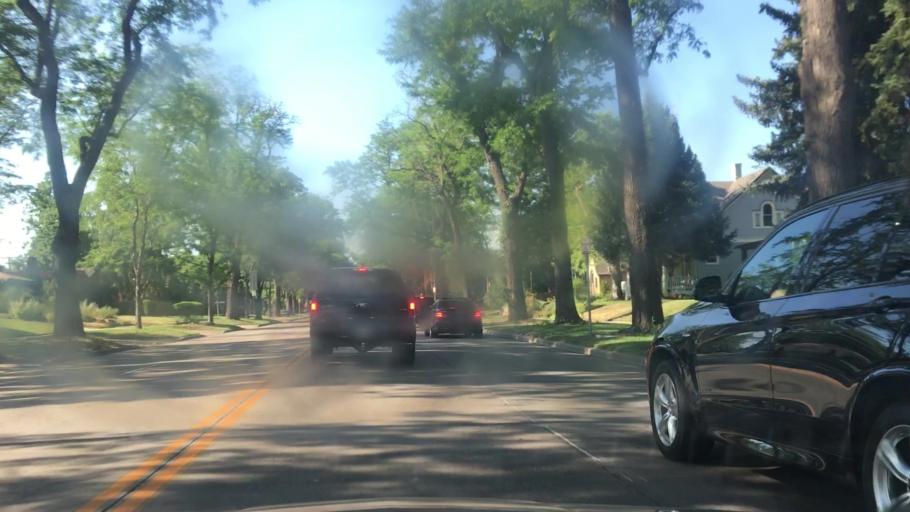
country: US
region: Colorado
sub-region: Arapahoe County
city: Glendale
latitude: 39.6979
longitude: -104.9593
